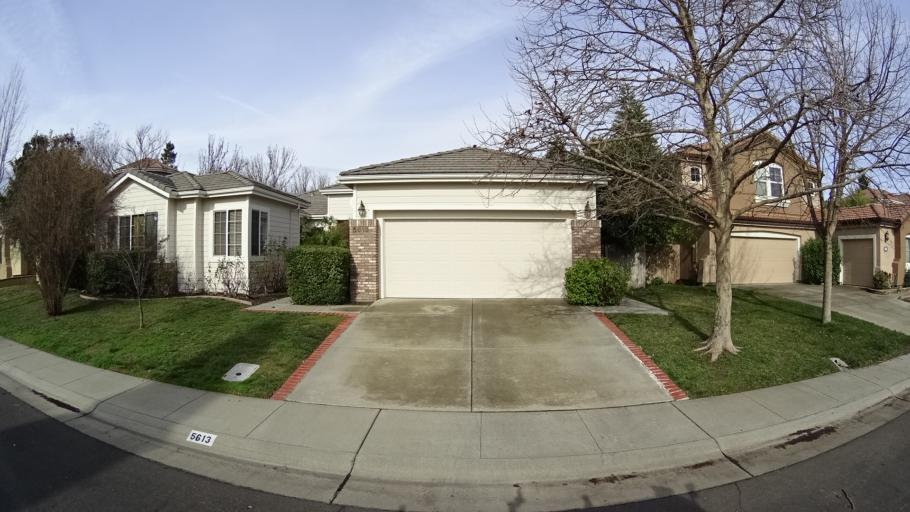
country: US
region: California
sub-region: Yolo County
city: Davis
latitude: 38.5514
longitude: -121.6782
